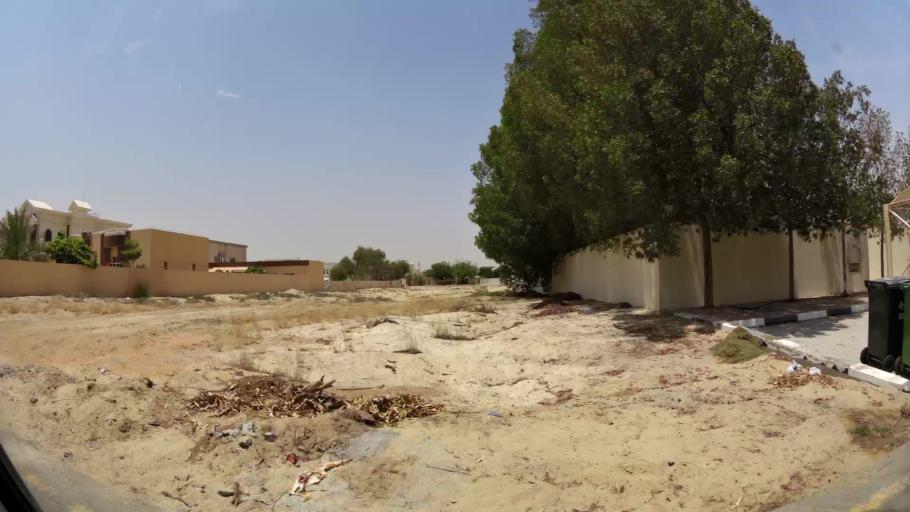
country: AE
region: Ash Shariqah
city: Sharjah
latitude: 25.2463
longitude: 55.4656
